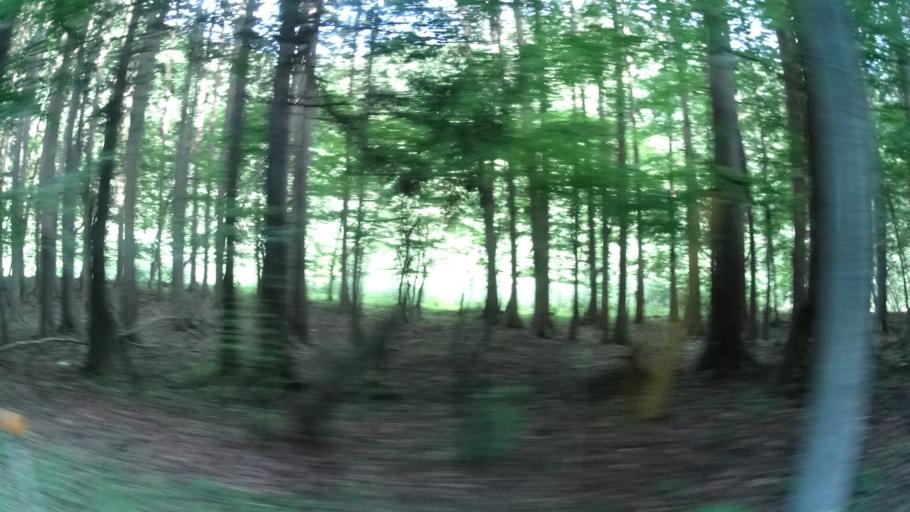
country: JP
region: Tochigi
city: Nikko
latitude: 36.6890
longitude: 139.4985
